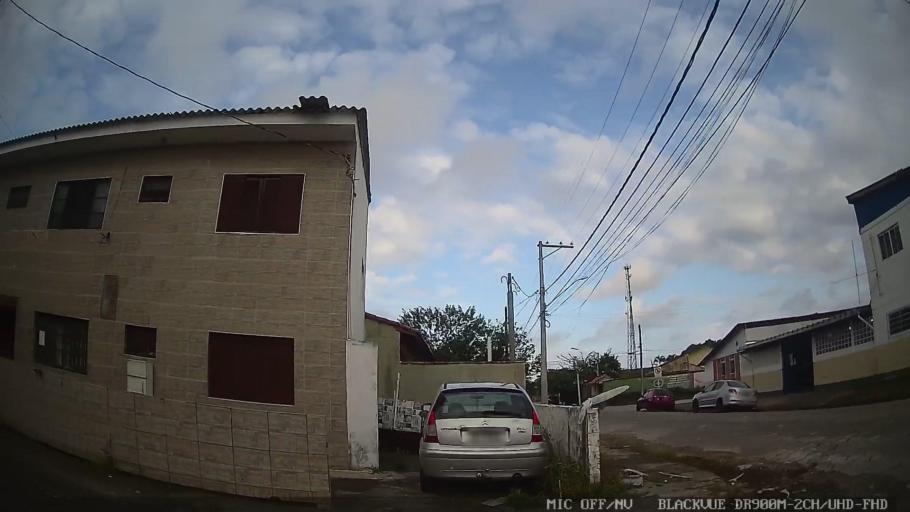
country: BR
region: Sao Paulo
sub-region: Itanhaem
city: Itanhaem
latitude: -24.1930
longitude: -46.8140
